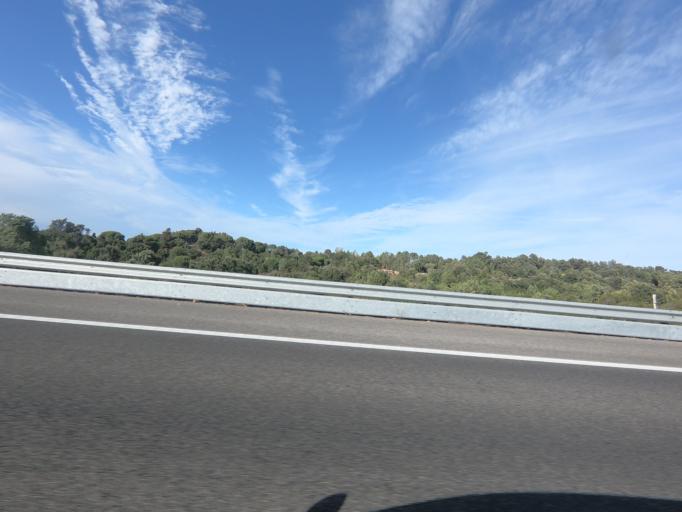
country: PT
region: Setubal
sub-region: Barreiro
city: Santo Antonio da Charneca
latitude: 38.5982
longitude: -9.0344
